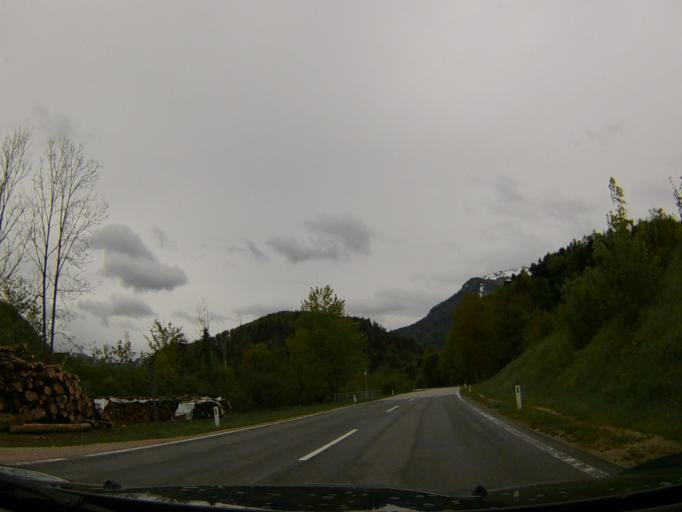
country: AT
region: Salzburg
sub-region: Politischer Bezirk Salzburg-Umgebung
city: Sankt Gilgen
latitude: 47.7817
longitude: 13.3851
